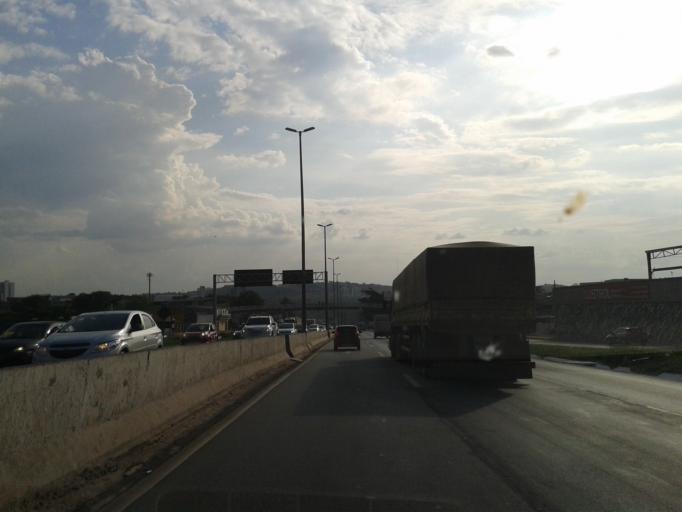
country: BR
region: Minas Gerais
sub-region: Belo Horizonte
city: Belo Horizonte
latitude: -19.8814
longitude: -43.9570
